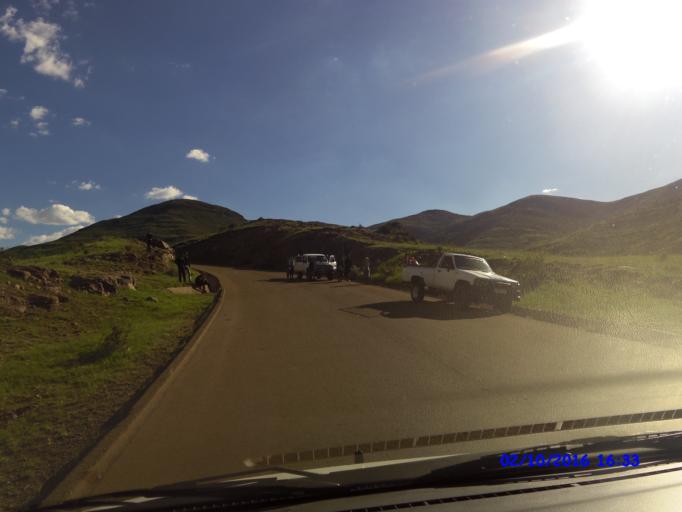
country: LS
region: Maseru
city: Nako
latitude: -29.4886
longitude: 28.0644
